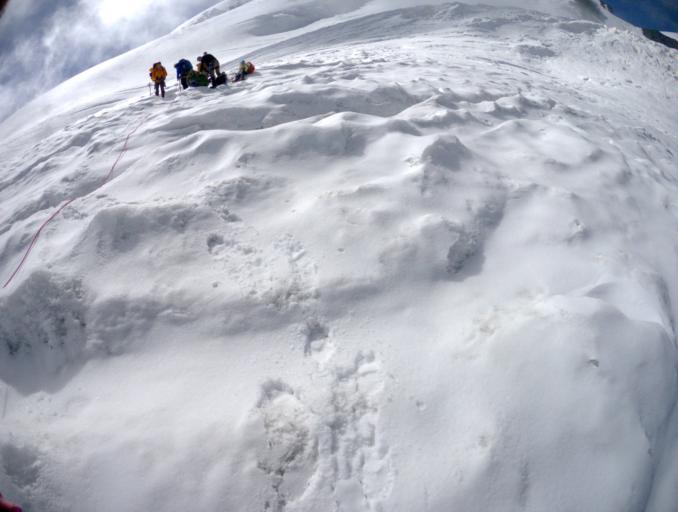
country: RU
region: Kabardino-Balkariya
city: Terskol
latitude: 43.3827
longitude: 42.4382
